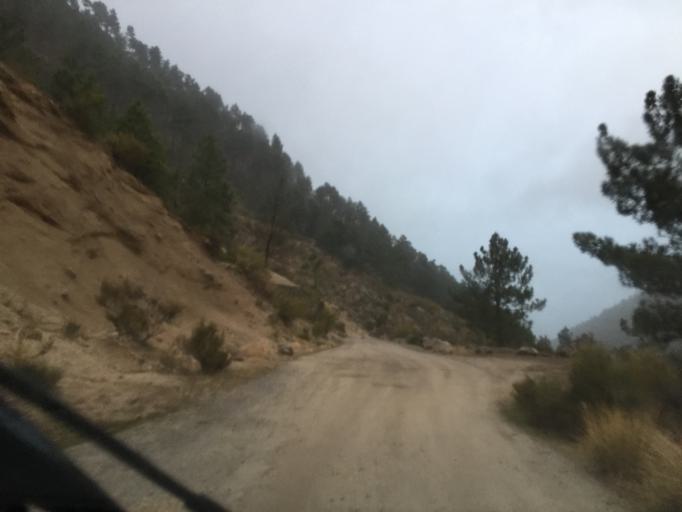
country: PT
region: Guarda
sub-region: Manteigas
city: Manteigas
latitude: 40.3664
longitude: -7.5543
